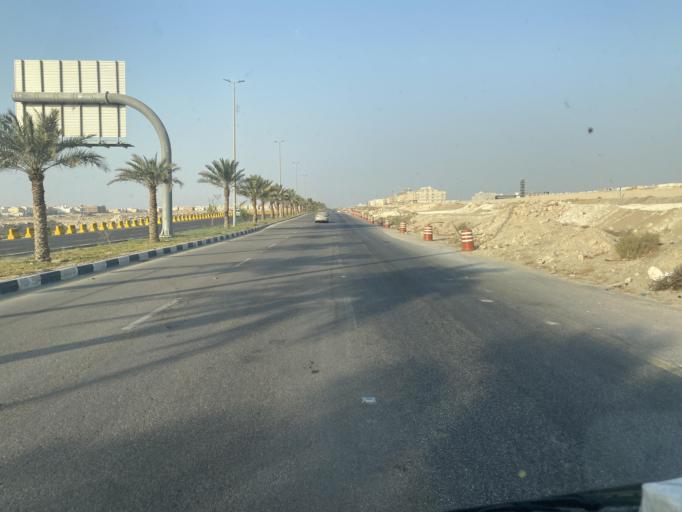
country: SA
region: Eastern Province
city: Dhahran
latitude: 26.3513
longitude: 50.0526
